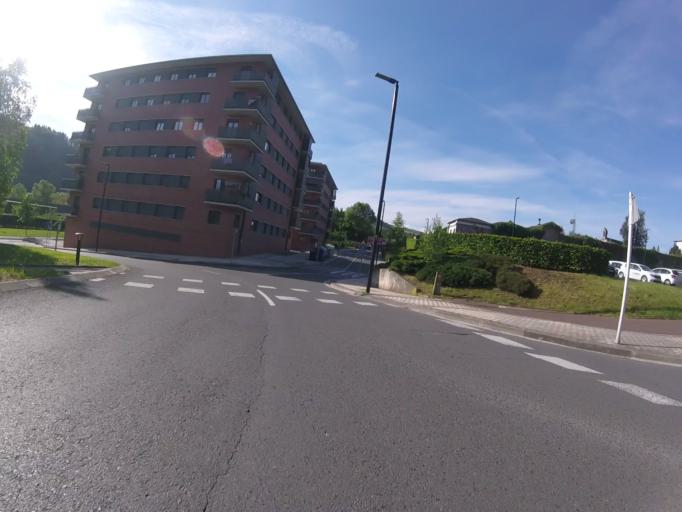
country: ES
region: Basque Country
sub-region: Provincia de Guipuzcoa
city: Villafranca de Ordizia
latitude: 43.0595
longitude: -2.1726
